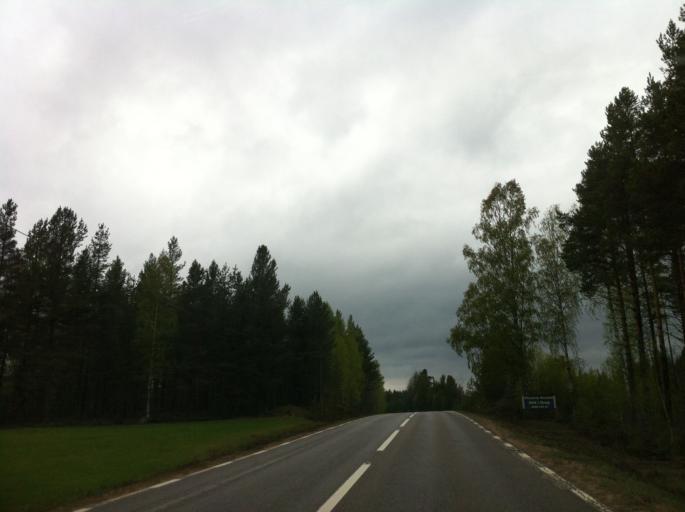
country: SE
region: Jaemtland
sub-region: Harjedalens Kommun
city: Sveg
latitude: 62.0269
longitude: 14.4336
